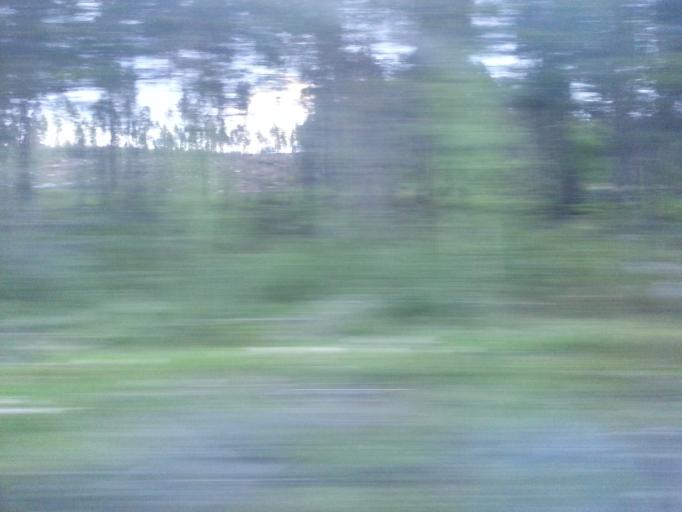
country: NO
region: Oppland
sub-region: Dovre
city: Dombas
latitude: 62.0930
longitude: 9.1382
